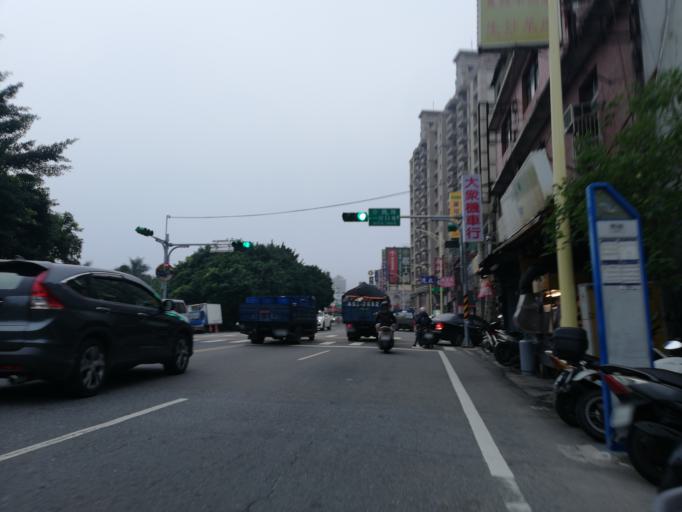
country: TW
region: Taiwan
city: Taoyuan City
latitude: 24.9768
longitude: 121.3029
